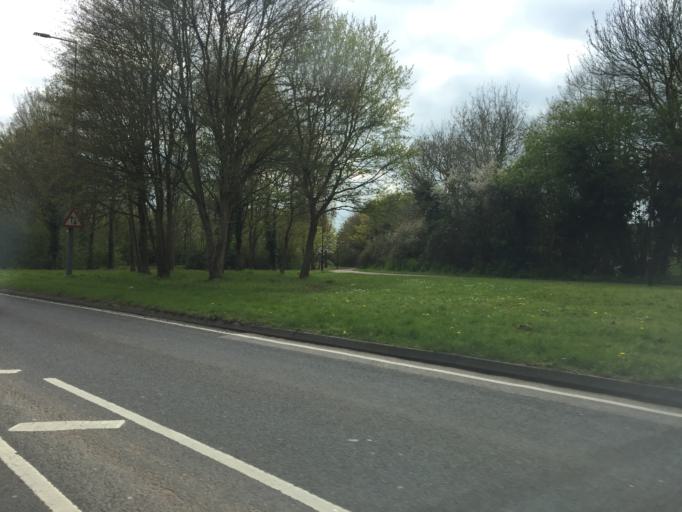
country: GB
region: England
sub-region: Milton Keynes
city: Milton Keynes
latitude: 52.0630
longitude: -0.7586
